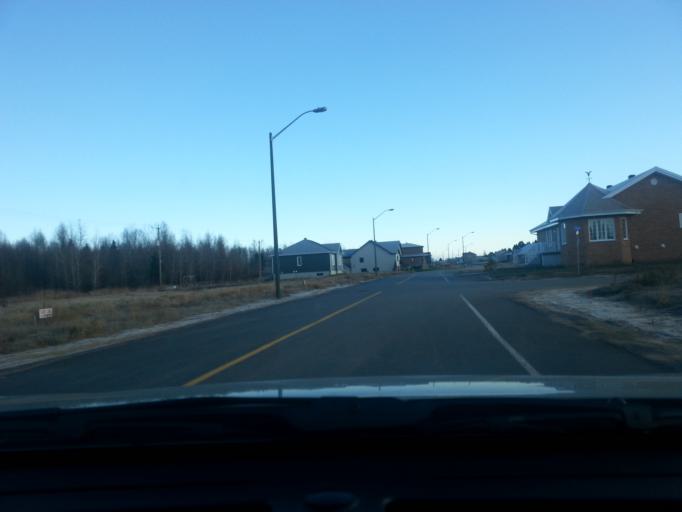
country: CA
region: Quebec
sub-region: Capitale-Nationale
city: Saint-Marc-des-Carrieres
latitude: 46.6834
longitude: -72.0718
